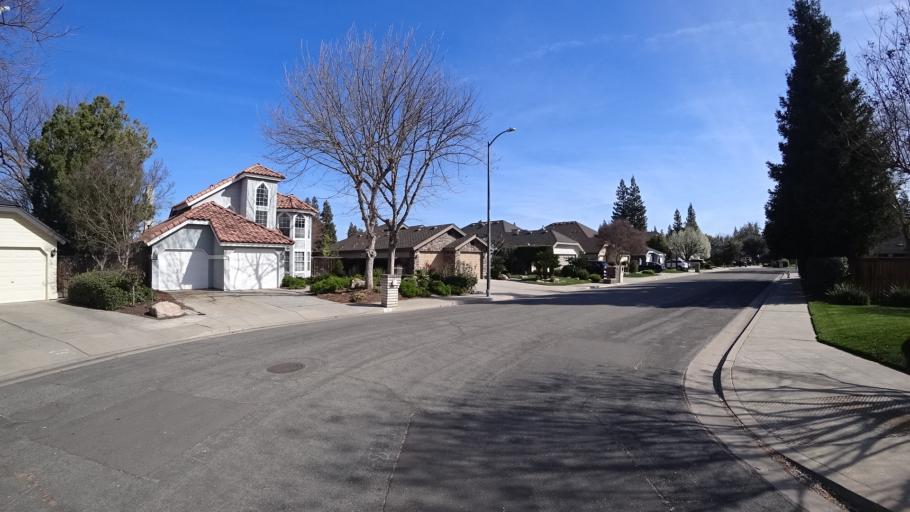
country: US
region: California
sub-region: Fresno County
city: Clovis
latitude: 36.8830
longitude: -119.7709
